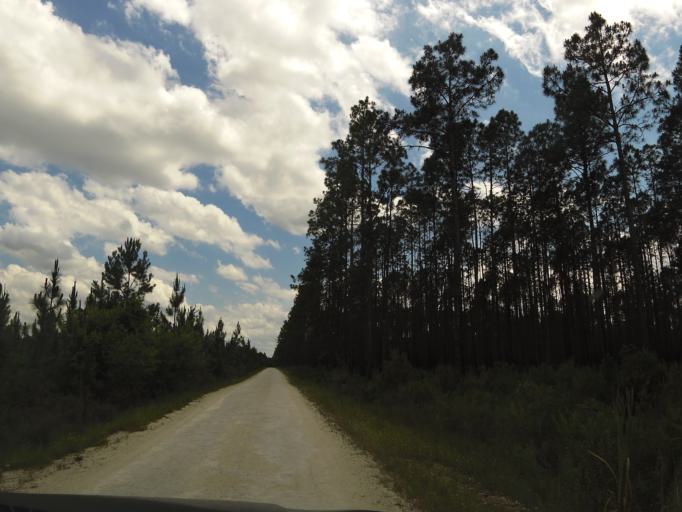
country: US
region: Florida
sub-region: Clay County
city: Asbury Lake
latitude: 29.8944
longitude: -81.8495
